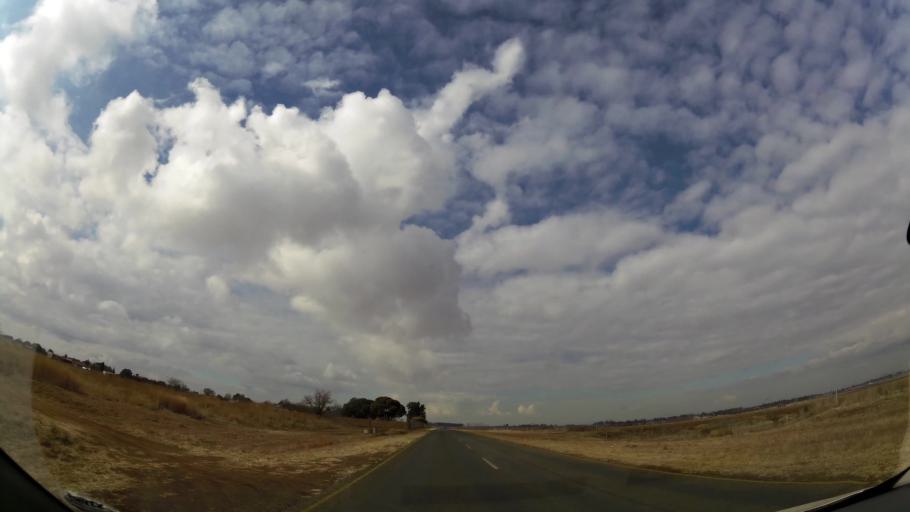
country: ZA
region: Gauteng
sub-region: Sedibeng District Municipality
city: Meyerton
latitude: -26.6124
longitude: 28.0497
